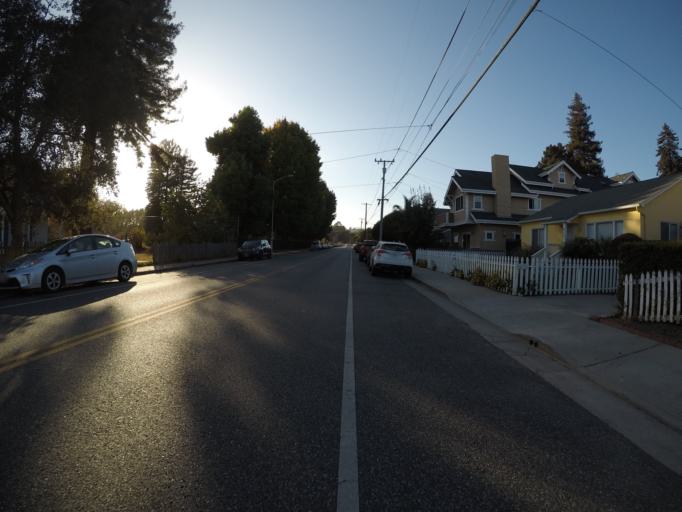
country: US
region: California
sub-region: Santa Cruz County
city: Santa Cruz
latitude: 36.9855
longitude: -122.0203
